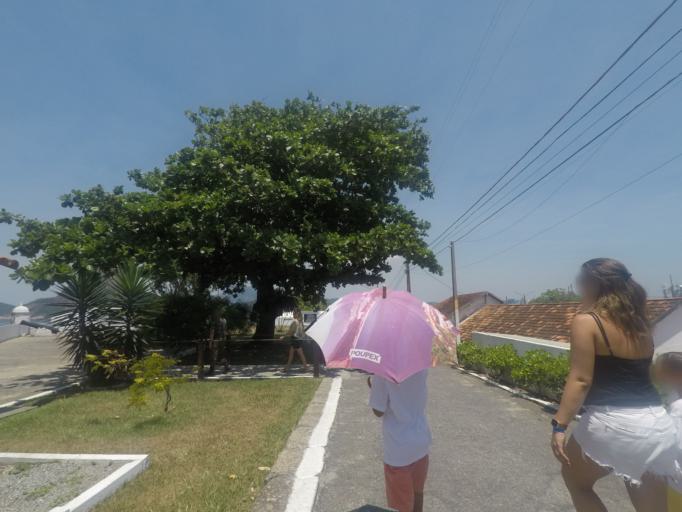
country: BR
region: Rio de Janeiro
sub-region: Niteroi
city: Niteroi
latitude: -22.9384
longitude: -43.1329
